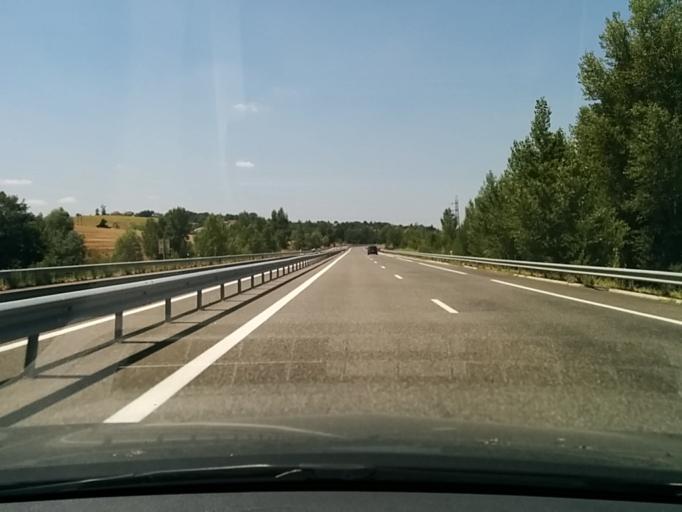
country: FR
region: Midi-Pyrenees
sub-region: Departement du Gers
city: Pujaudran
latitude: 43.5998
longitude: 1.0930
